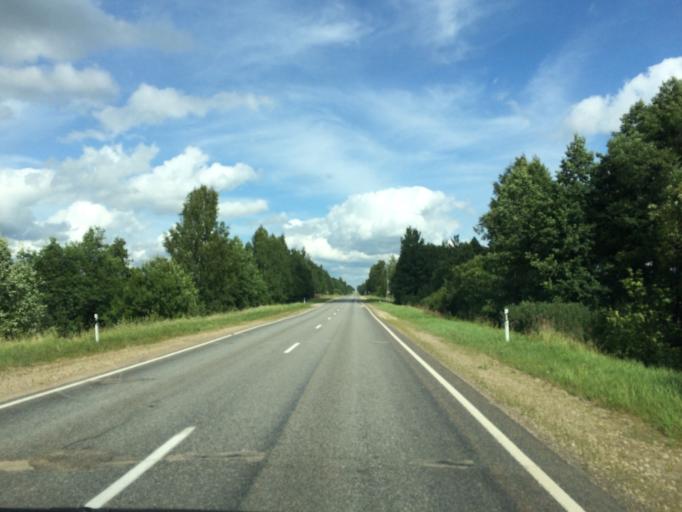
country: LV
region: Rezekne
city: Rezekne
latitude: 56.6393
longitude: 27.4791
